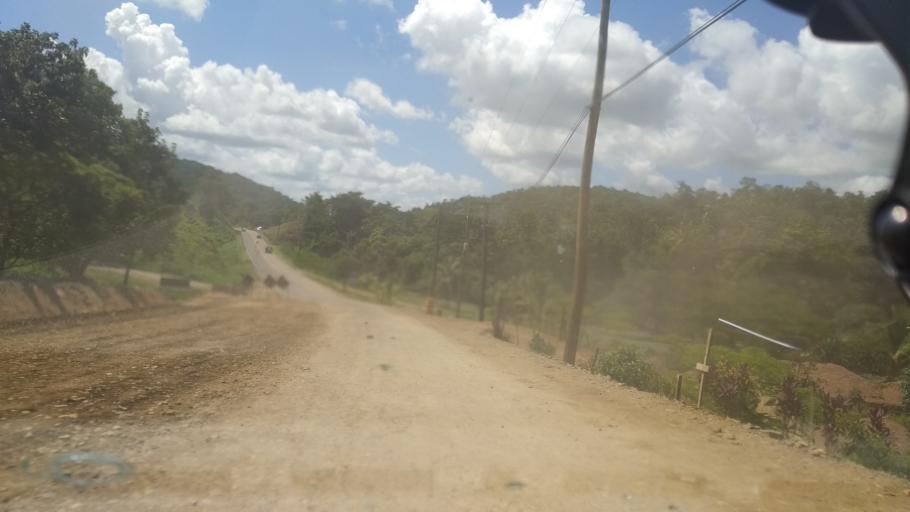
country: BZ
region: Cayo
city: Belmopan
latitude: 17.0694
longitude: -88.5914
